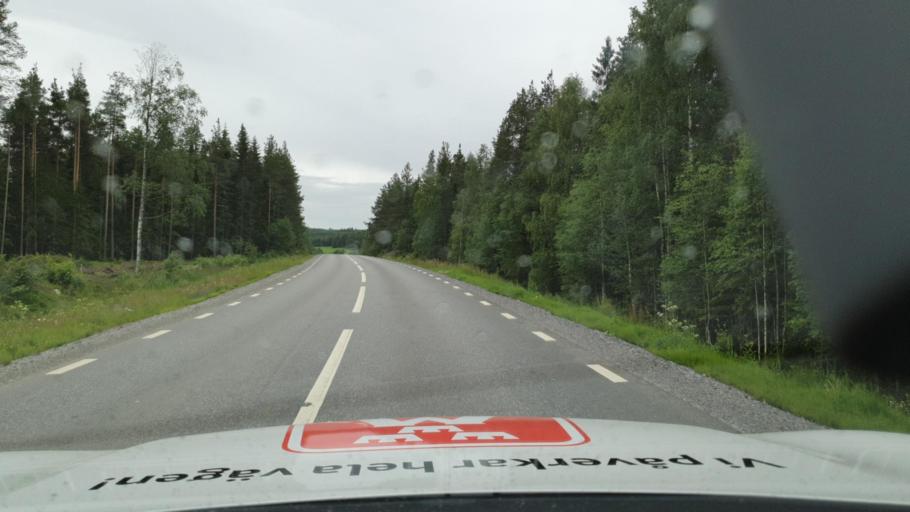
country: SE
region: Vaesterbotten
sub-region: Skelleftea Kommun
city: Burtraesk
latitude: 64.3740
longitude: 20.5055
